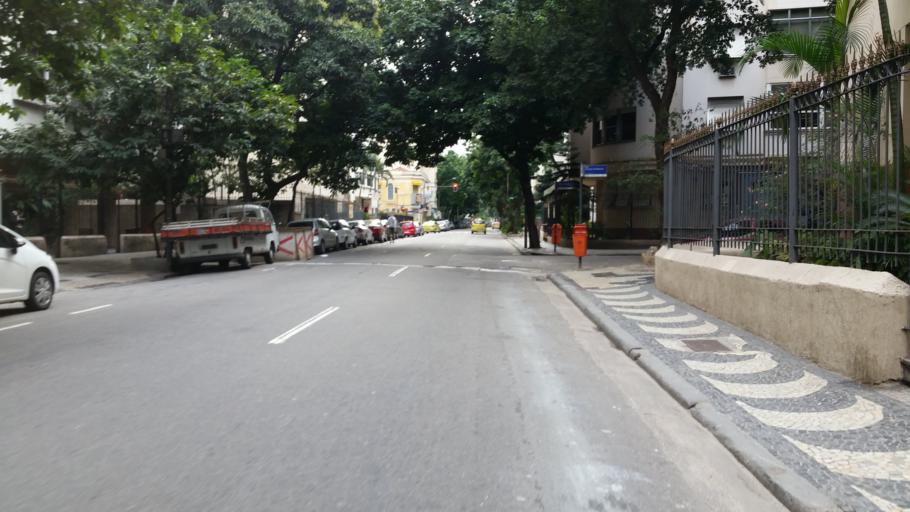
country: BR
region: Rio de Janeiro
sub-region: Rio De Janeiro
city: Rio de Janeiro
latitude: -22.9393
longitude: -43.1768
